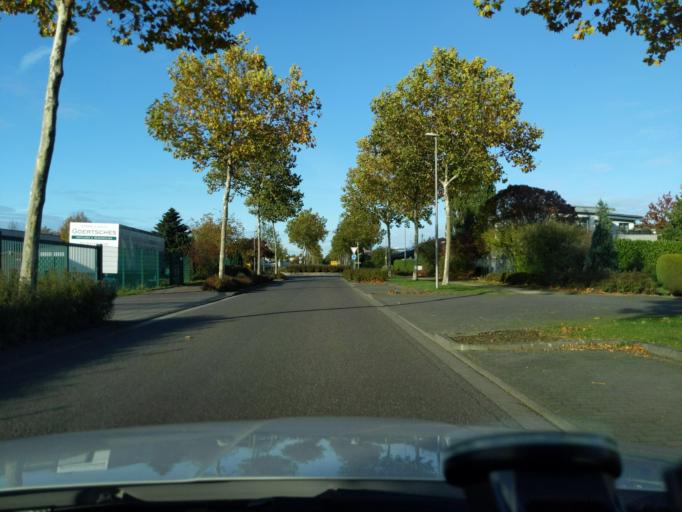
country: DE
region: North Rhine-Westphalia
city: Kempen
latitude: 51.3663
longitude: 6.4399
